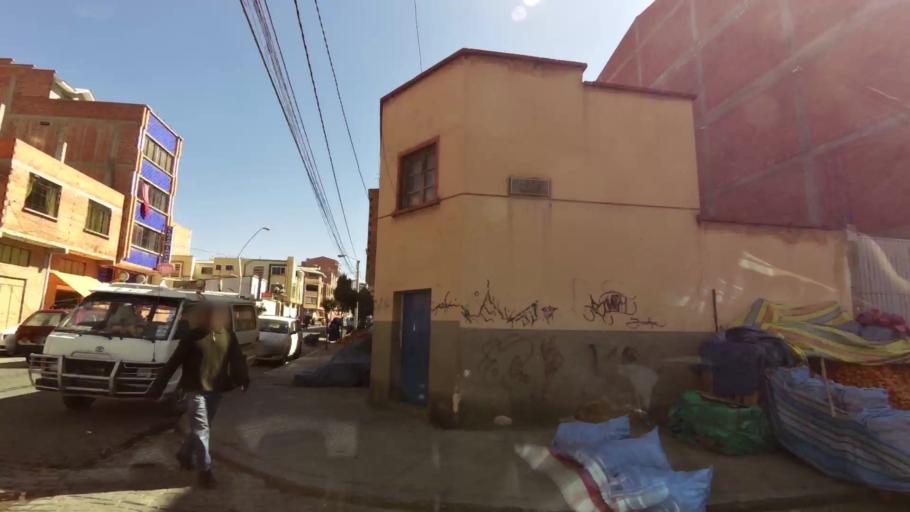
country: BO
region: La Paz
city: La Paz
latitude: -16.5122
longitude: -68.1564
